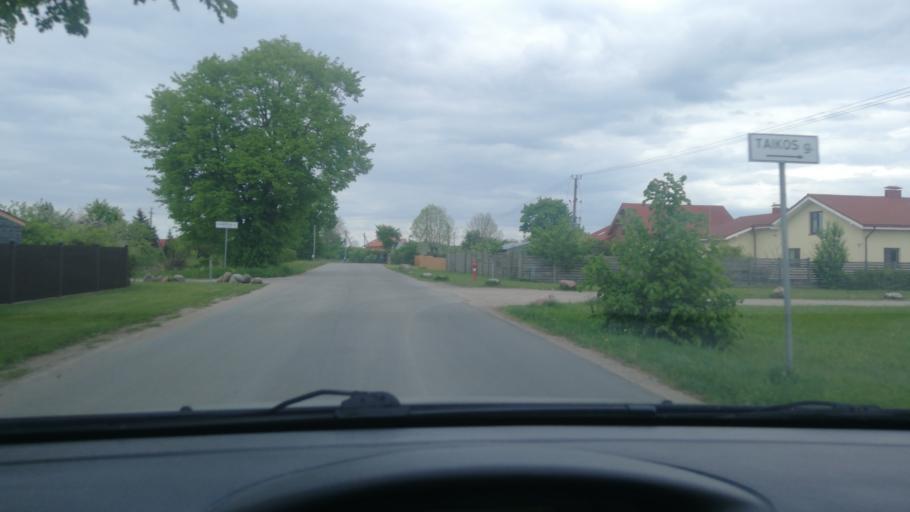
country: LT
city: Priekule
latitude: 55.6444
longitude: 21.2962
